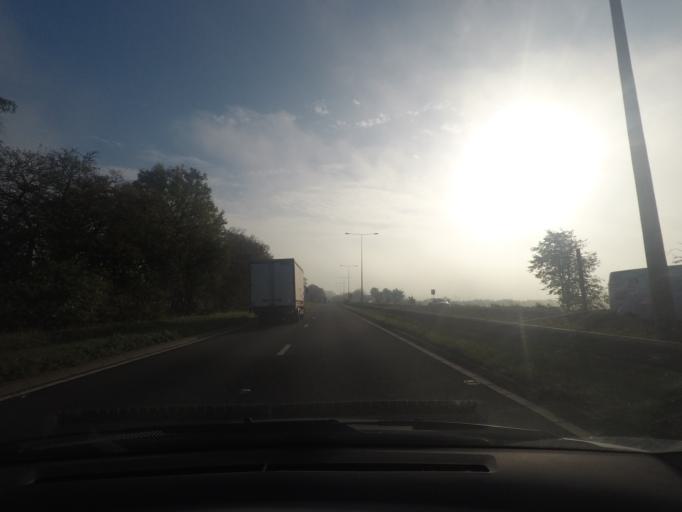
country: GB
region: England
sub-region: East Riding of Yorkshire
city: Welton
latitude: 53.7280
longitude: -0.5421
